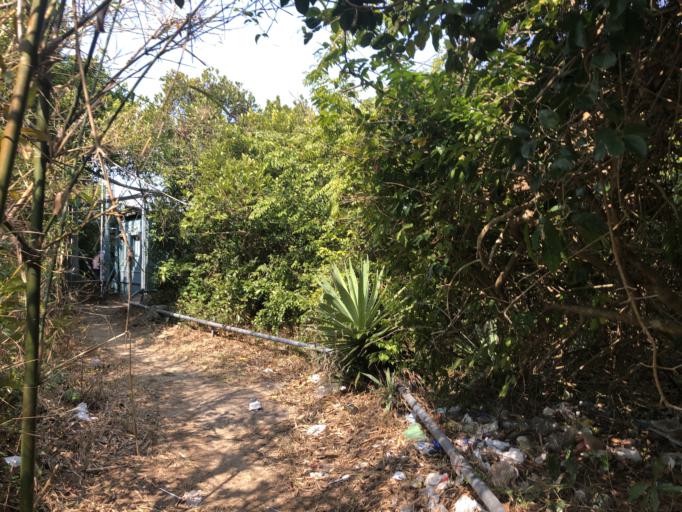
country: HK
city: Sok Kwu Wan
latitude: 22.1648
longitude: 114.2514
